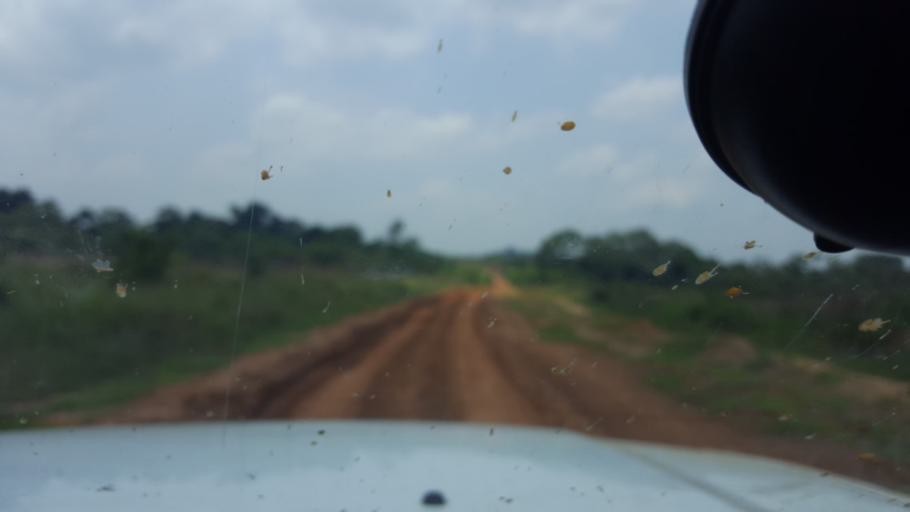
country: CD
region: Bandundu
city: Mushie
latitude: -3.7468
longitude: 16.6574
